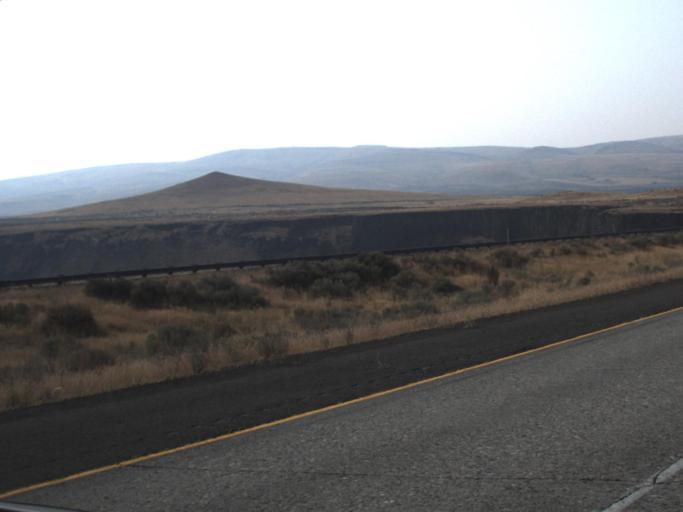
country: US
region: Washington
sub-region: Yakima County
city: Terrace Heights
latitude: 46.7039
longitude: -120.4392
